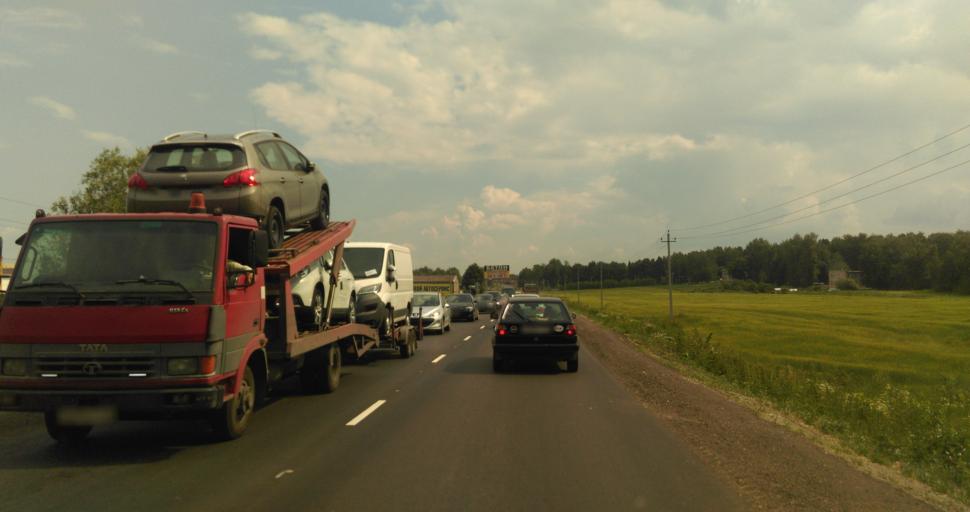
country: RU
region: Moskovskaya
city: Zhitnevo
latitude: 55.3502
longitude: 37.8979
